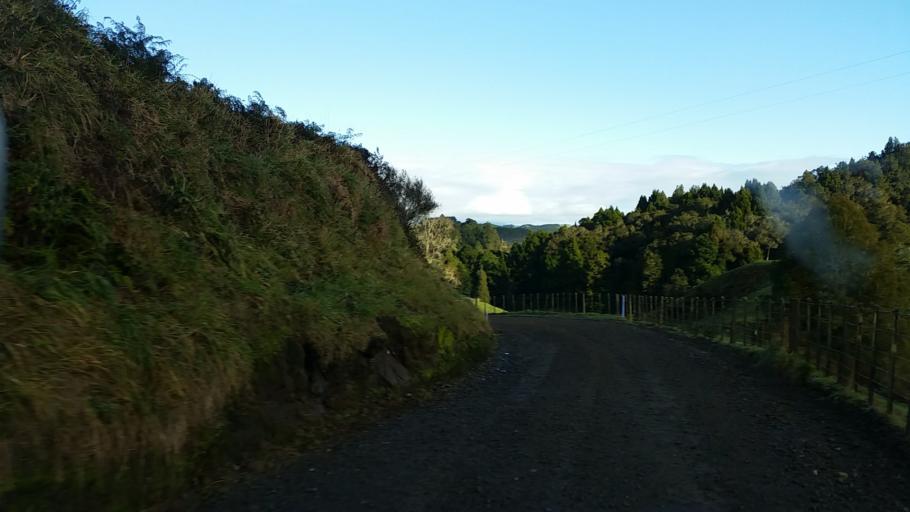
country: NZ
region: Taranaki
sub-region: South Taranaki District
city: Eltham
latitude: -39.2476
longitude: 174.3809
